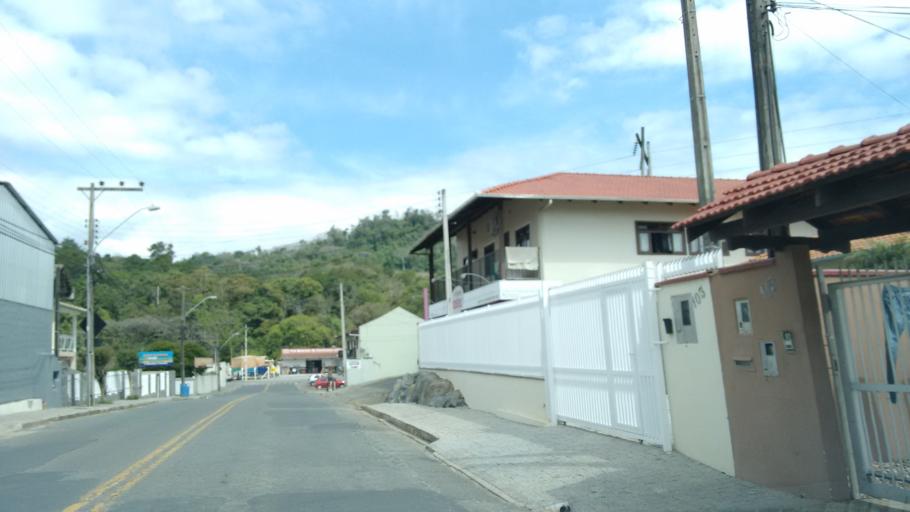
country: BR
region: Santa Catarina
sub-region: Blumenau
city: Blumenau
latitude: -26.8628
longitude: -49.1262
